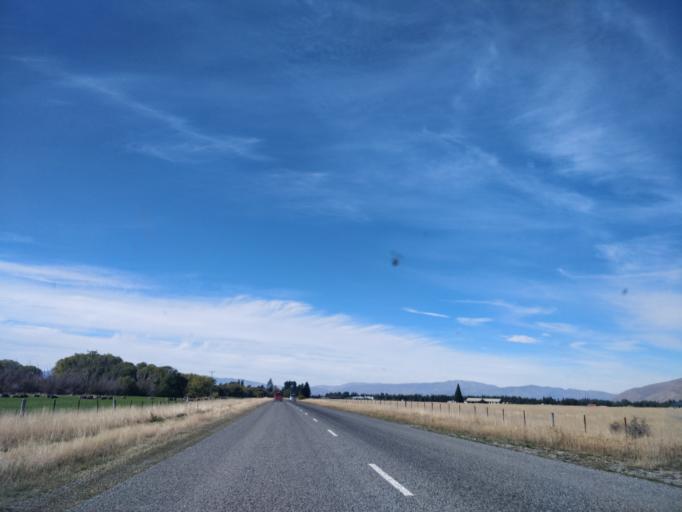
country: NZ
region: Otago
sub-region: Queenstown-Lakes District
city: Wanaka
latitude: -44.2358
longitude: 170.0726
